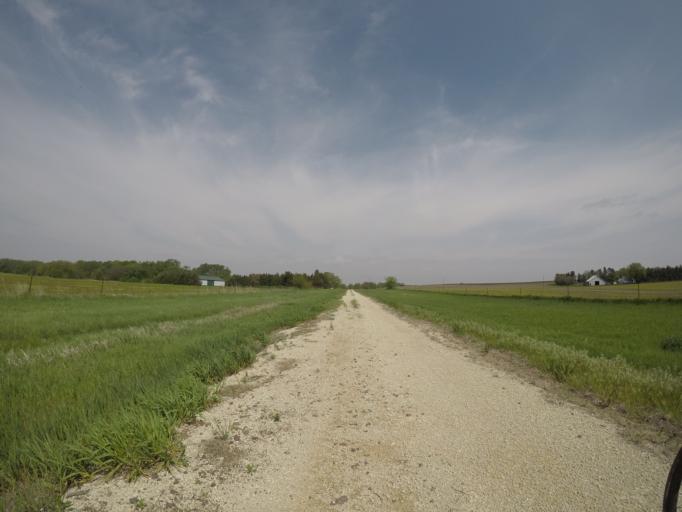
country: US
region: Nebraska
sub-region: Gage County
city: Wymore
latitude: 40.1662
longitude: -96.6455
